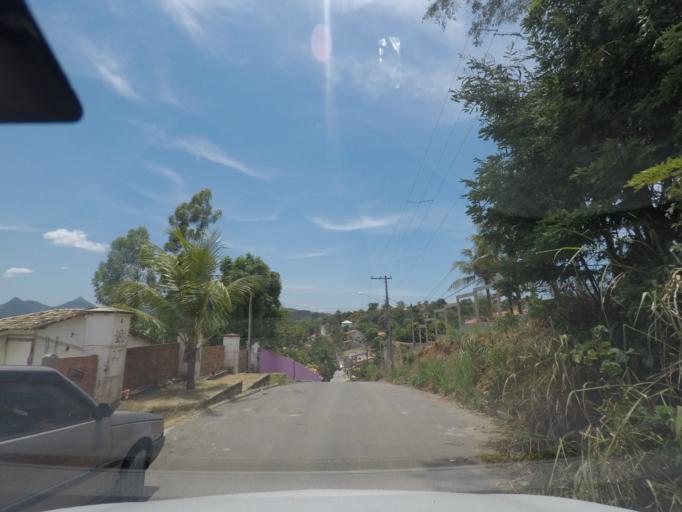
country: BR
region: Rio de Janeiro
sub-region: Marica
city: Marica
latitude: -22.9246
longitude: -42.8263
